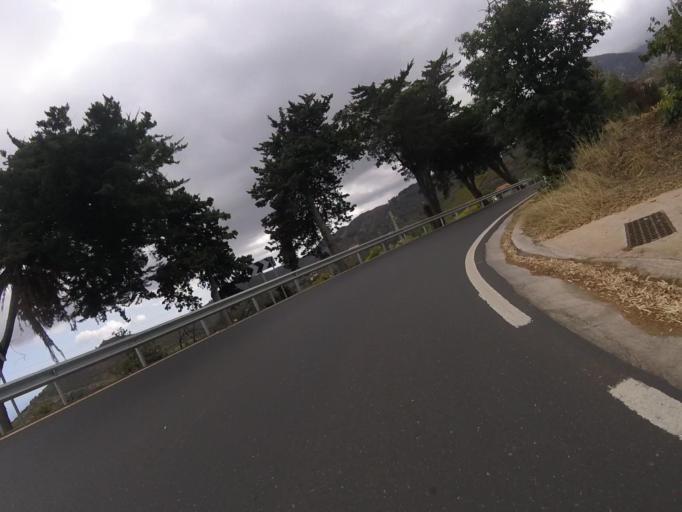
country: ES
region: Canary Islands
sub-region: Provincia de Las Palmas
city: Vega de San Mateo
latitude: 28.0097
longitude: -15.5488
